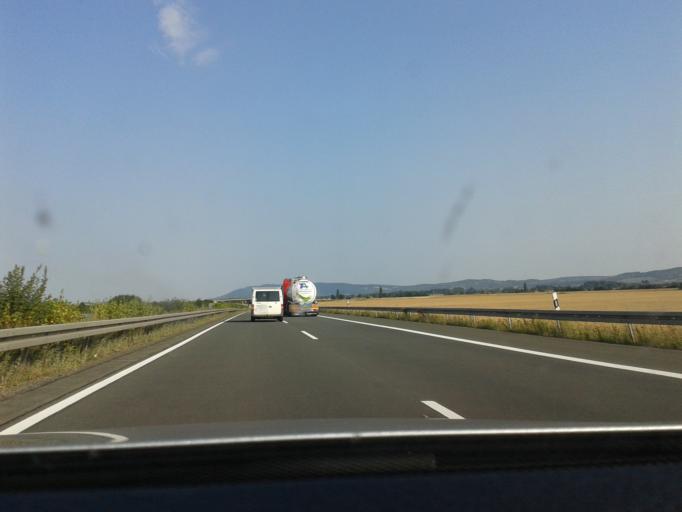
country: DE
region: Thuringia
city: Urbach
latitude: 51.4743
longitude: 10.8864
